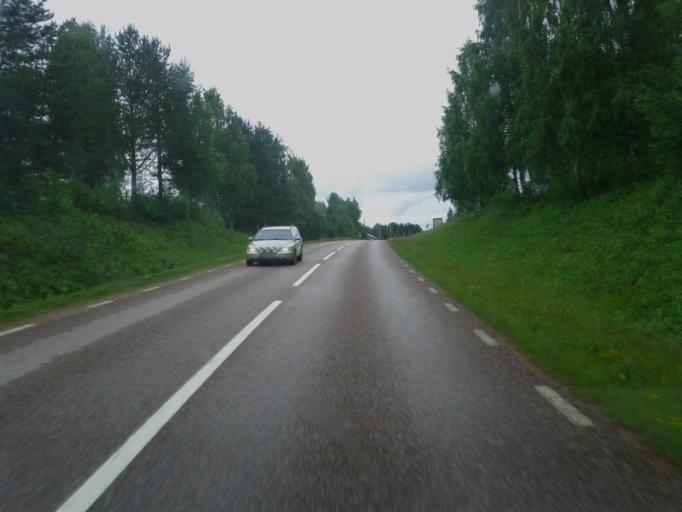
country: NO
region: Hedmark
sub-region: Trysil
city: Innbygda
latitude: 61.7324
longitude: 12.9860
